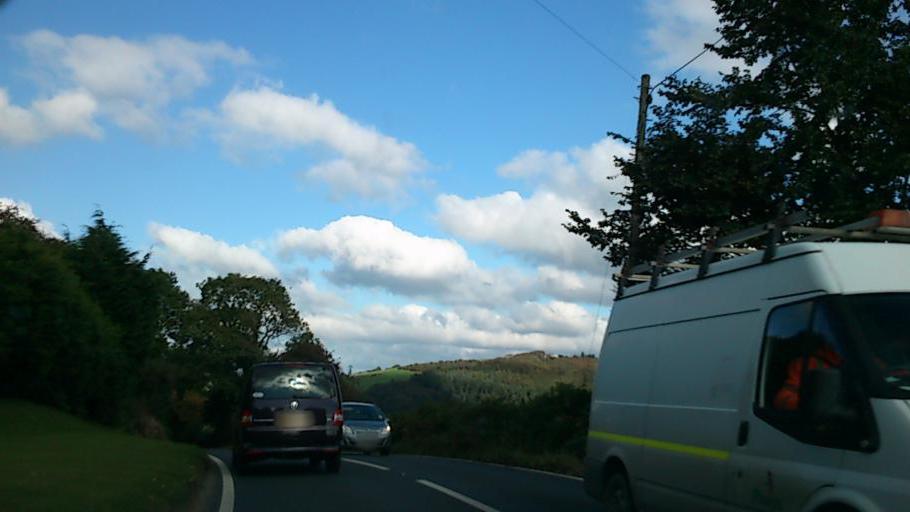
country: GB
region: Wales
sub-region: County of Ceredigion
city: Bow Street
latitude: 52.4285
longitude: -4.0325
